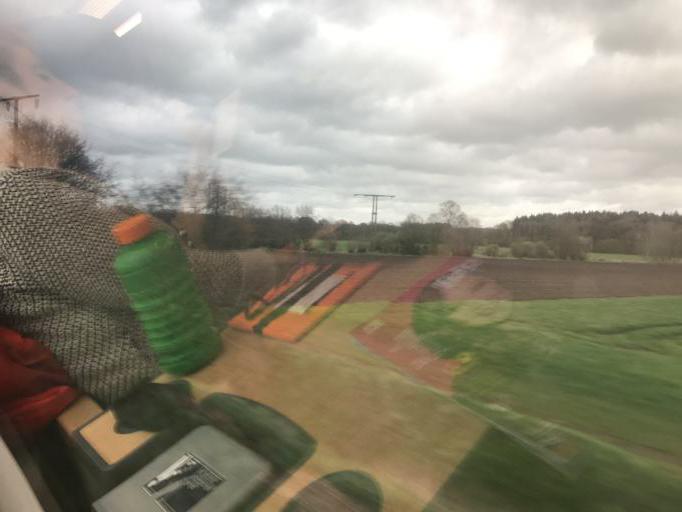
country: DE
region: Schleswig-Holstein
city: Quarnstedt
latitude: 53.9687
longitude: 9.7824
